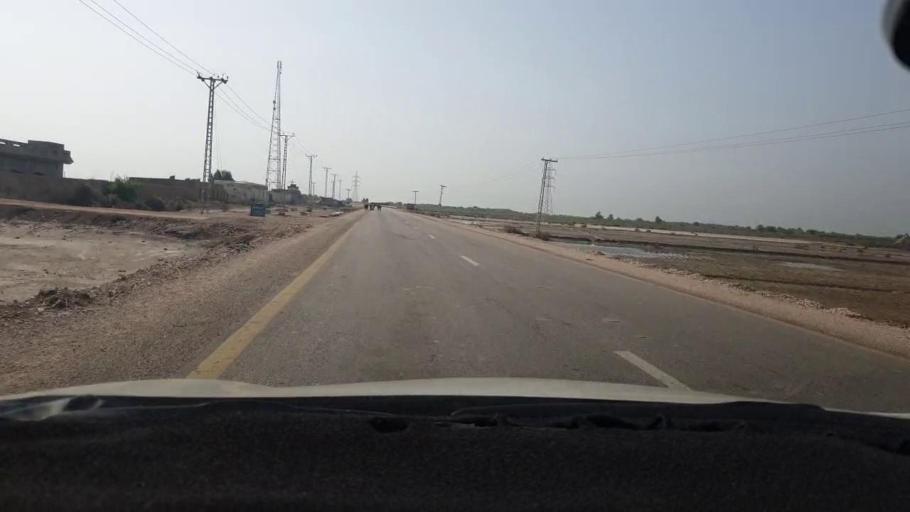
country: PK
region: Sindh
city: Jhol
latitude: 25.9561
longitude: 68.9758
